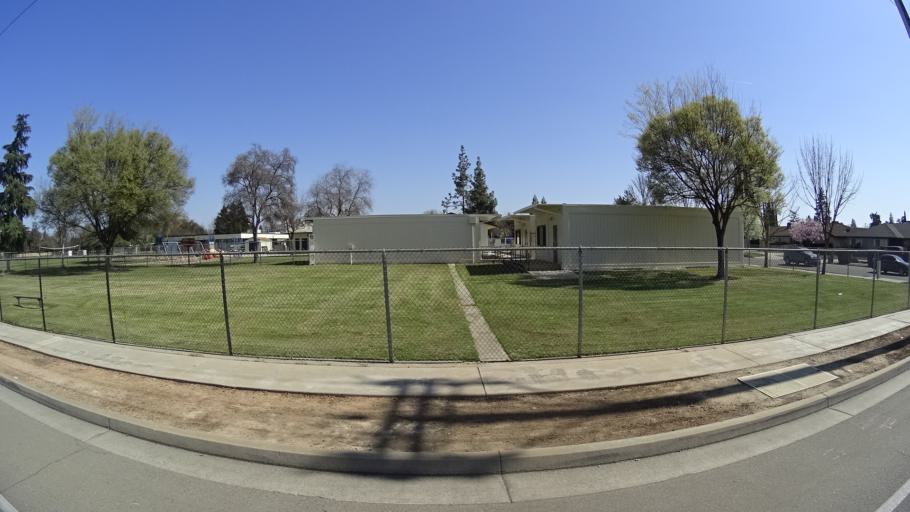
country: US
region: California
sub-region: Fresno County
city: Fresno
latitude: 36.8302
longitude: -119.8263
